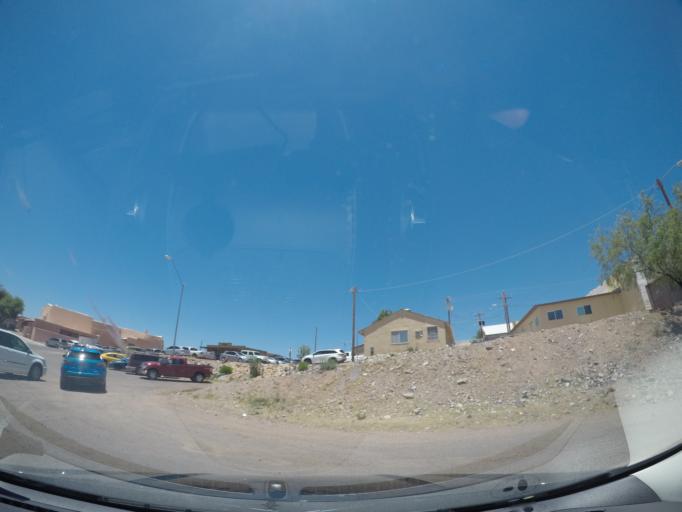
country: US
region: Arizona
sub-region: Cochise County
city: Tombstone
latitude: 31.7113
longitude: -110.0648
